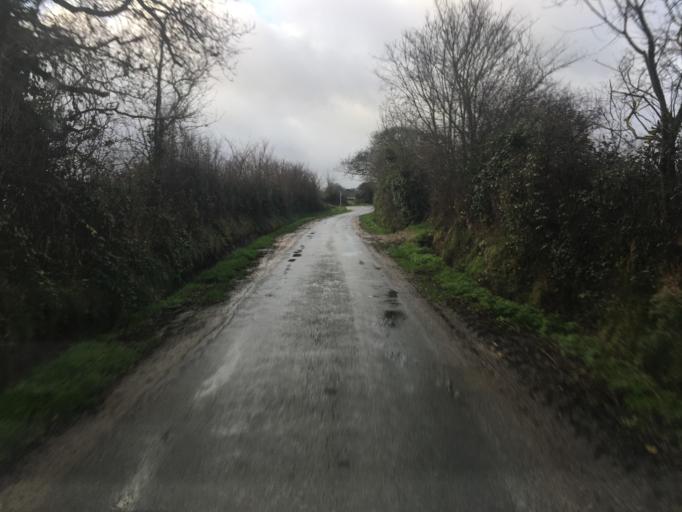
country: FR
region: Lower Normandy
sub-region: Departement de la Manche
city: Saint-Pierre-Eglise
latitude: 49.6715
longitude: -1.3238
